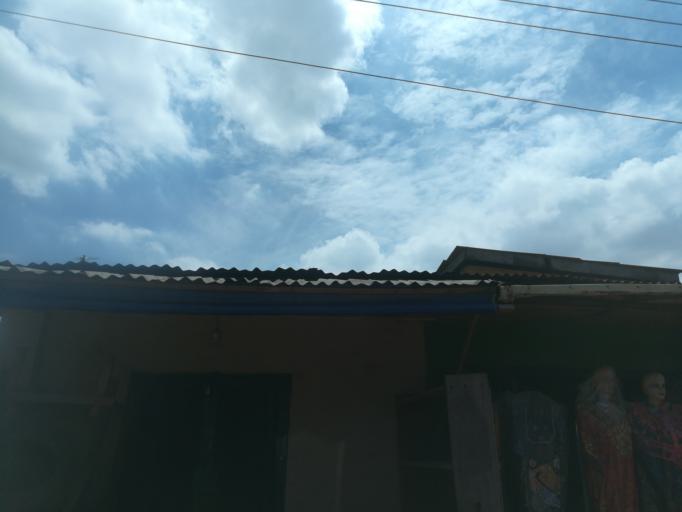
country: NG
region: Lagos
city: Oshodi
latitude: 6.5659
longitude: 3.3360
